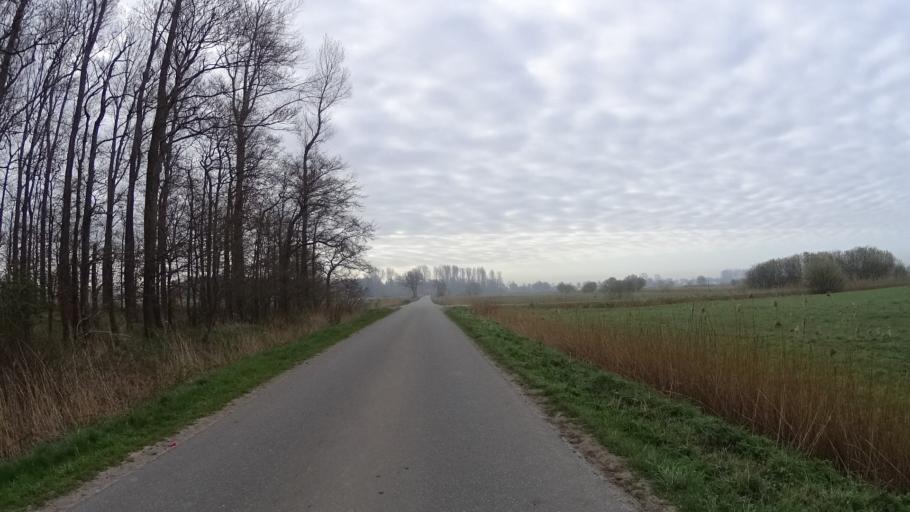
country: DE
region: Lower Saxony
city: Upgant-Schott
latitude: 53.4543
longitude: 7.3293
